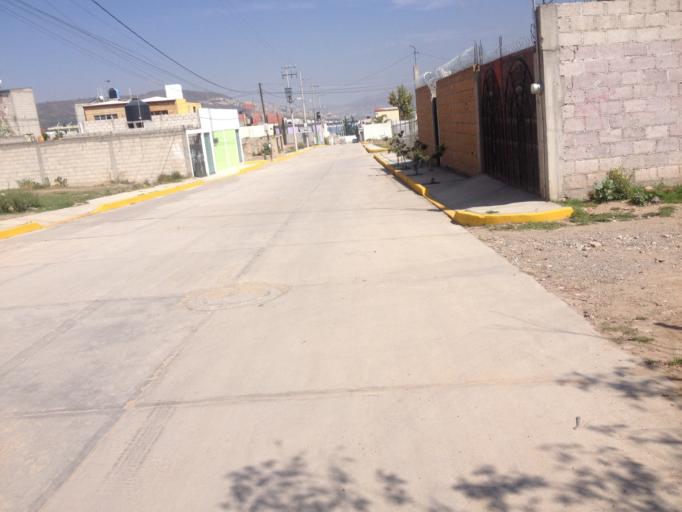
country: MX
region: Hidalgo
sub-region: Mineral de la Reforma
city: Carboneras
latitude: 20.0923
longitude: -98.7039
